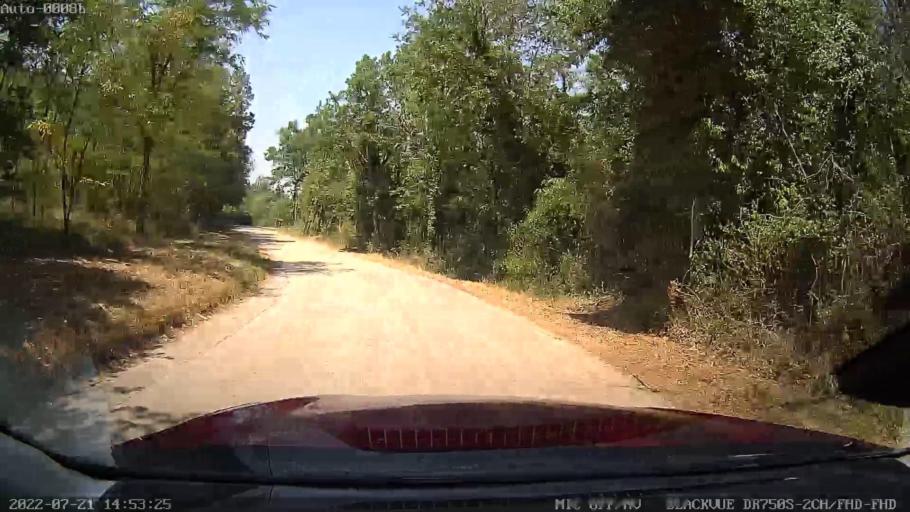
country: HR
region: Istarska
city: Pazin
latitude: 45.1816
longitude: 13.9318
